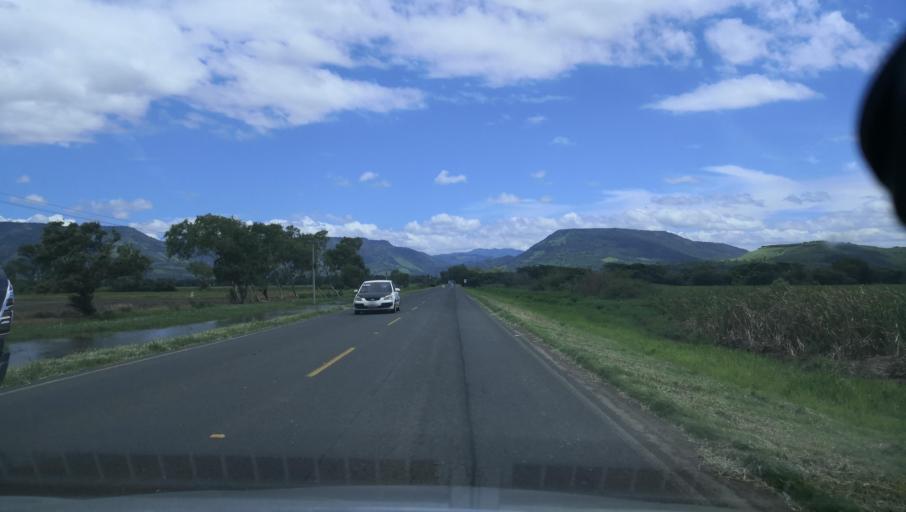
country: NI
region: Matagalpa
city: Ciudad Dario
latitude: 12.9004
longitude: -86.1611
